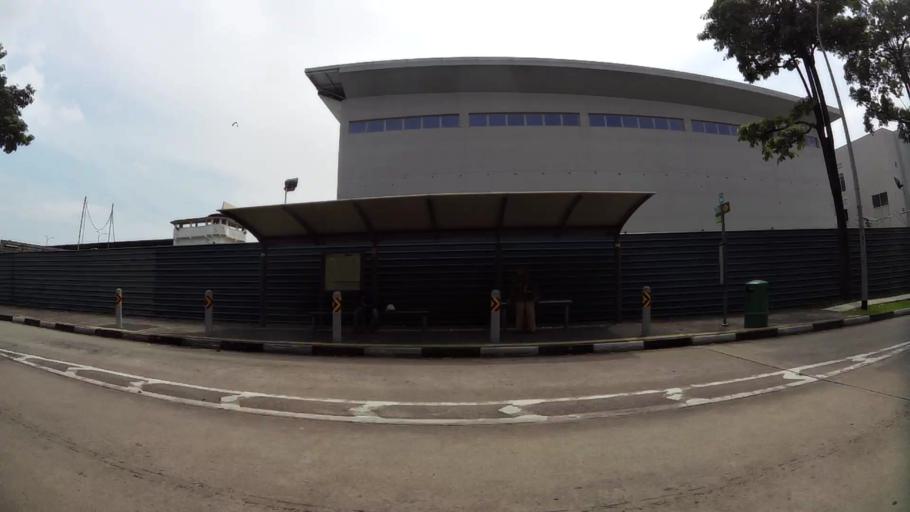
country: SG
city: Singapore
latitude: 1.3554
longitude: 103.9689
